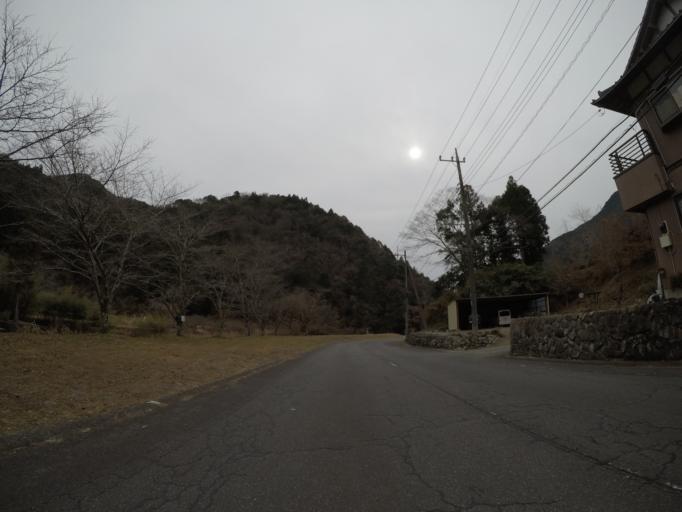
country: JP
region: Shizuoka
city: Fujinomiya
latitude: 35.2655
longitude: 138.5306
